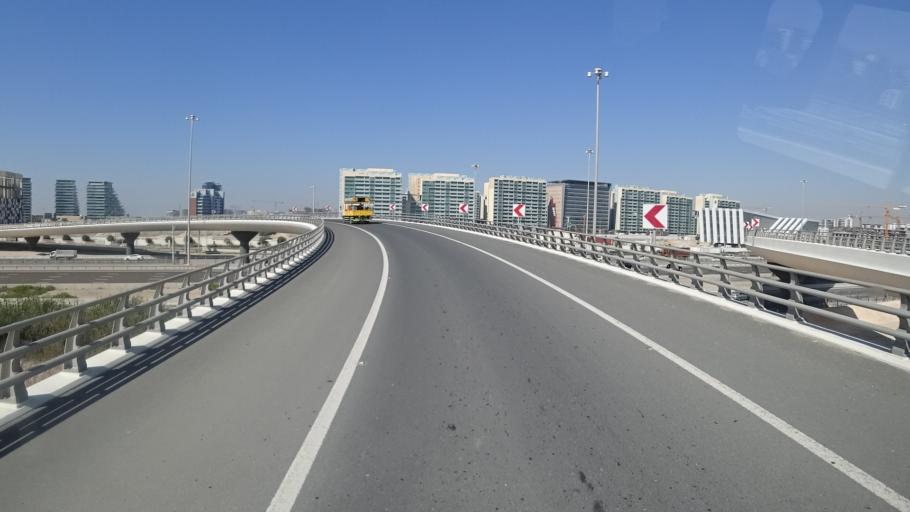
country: AE
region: Abu Dhabi
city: Abu Dhabi
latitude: 24.4449
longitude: 54.6039
